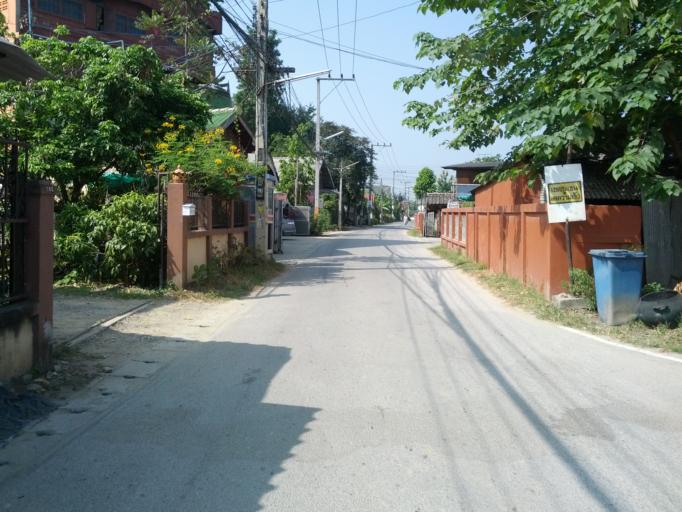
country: TH
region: Chiang Mai
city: San Kamphaeng
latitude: 18.7729
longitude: 99.0783
